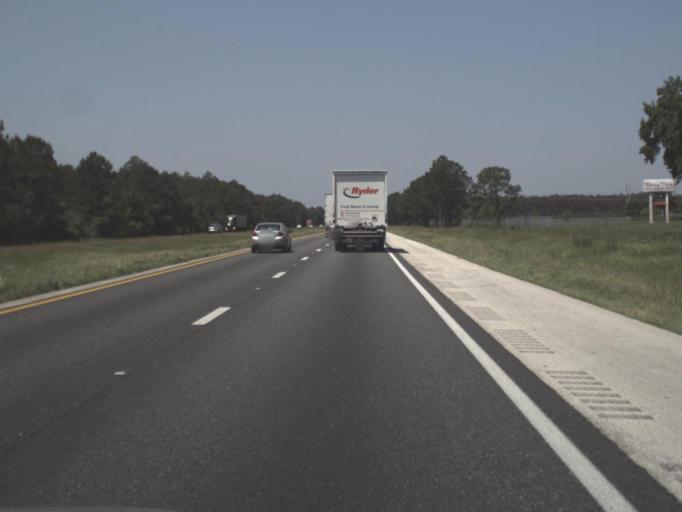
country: US
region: Florida
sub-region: Duval County
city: Baldwin
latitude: 30.2967
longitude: -81.9410
